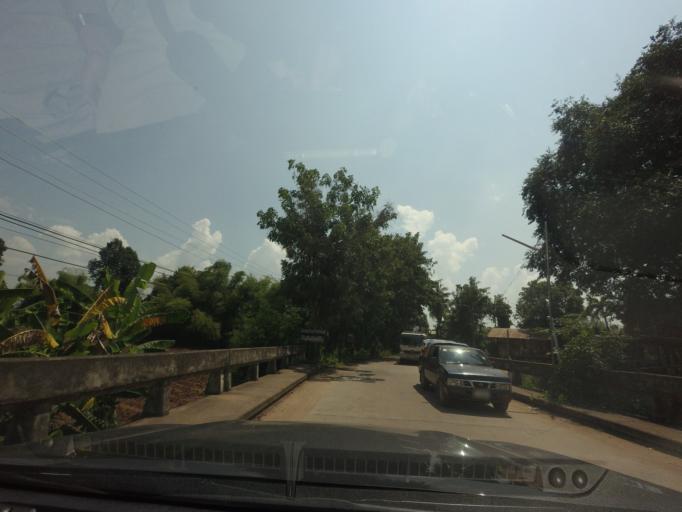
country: TH
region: Uttaradit
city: Thong Saen Khan
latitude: 17.4593
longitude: 100.3081
